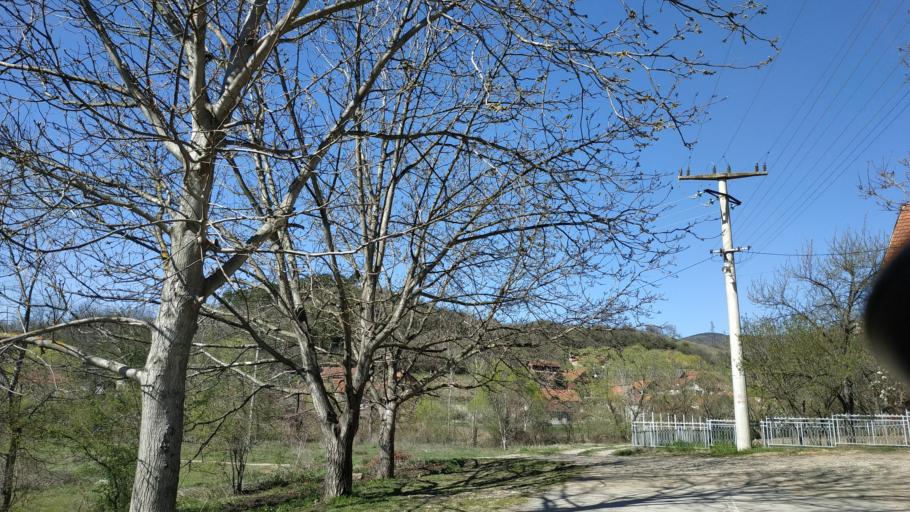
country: RS
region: Central Serbia
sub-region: Nisavski Okrug
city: Aleksinac
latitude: 43.5490
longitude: 21.7119
